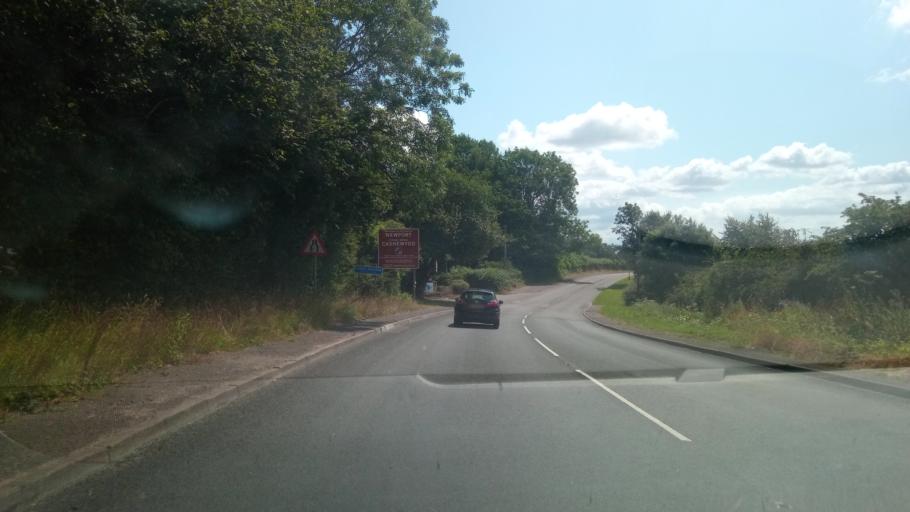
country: GB
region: Wales
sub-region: Caerphilly County Borough
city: Machen
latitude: 51.5895
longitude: -3.1234
